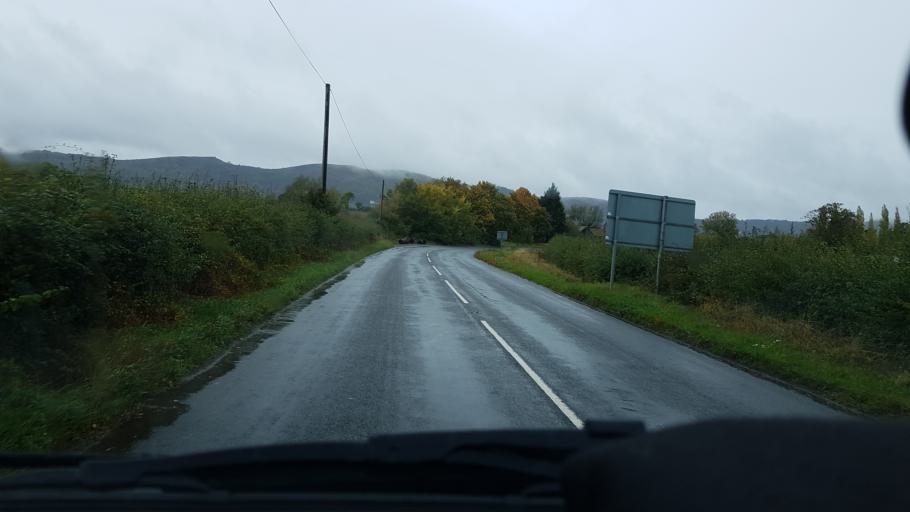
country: GB
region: England
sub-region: Worcestershire
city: Great Malvern
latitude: 52.0682
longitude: -2.2960
